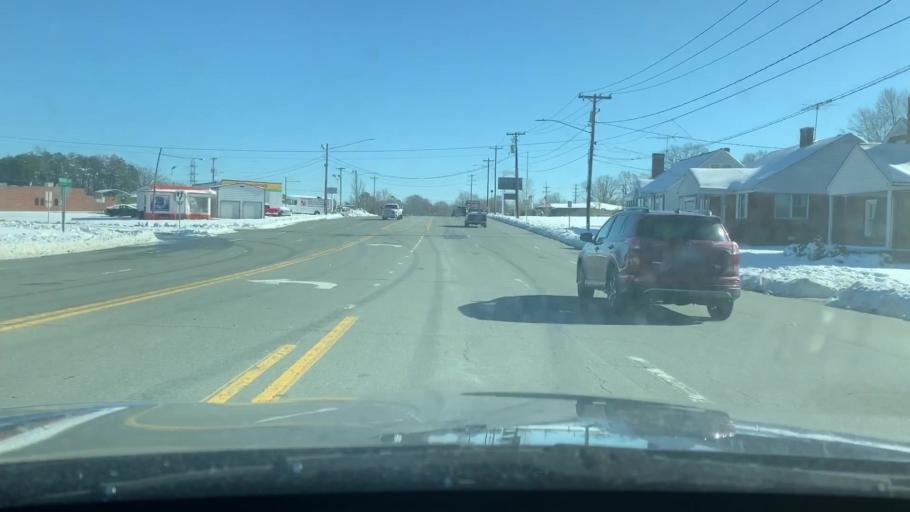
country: US
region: North Carolina
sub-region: Alamance County
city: Burlington
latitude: 36.0997
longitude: -79.4212
